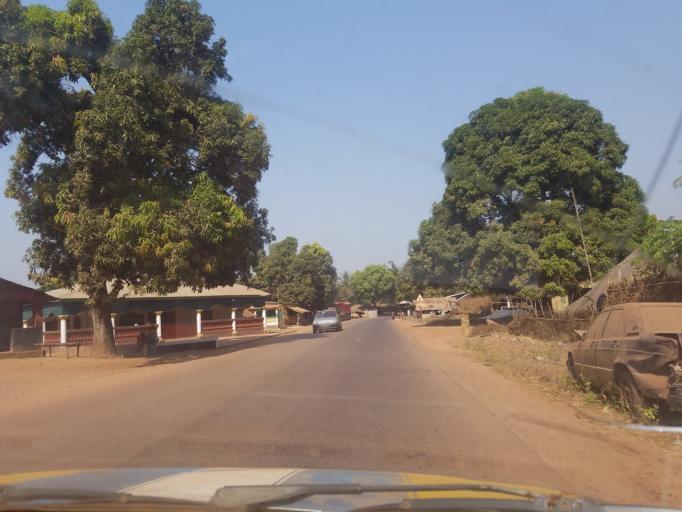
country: GN
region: Boke
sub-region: Boke Prefecture
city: Boke
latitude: 10.8330
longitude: -14.3656
